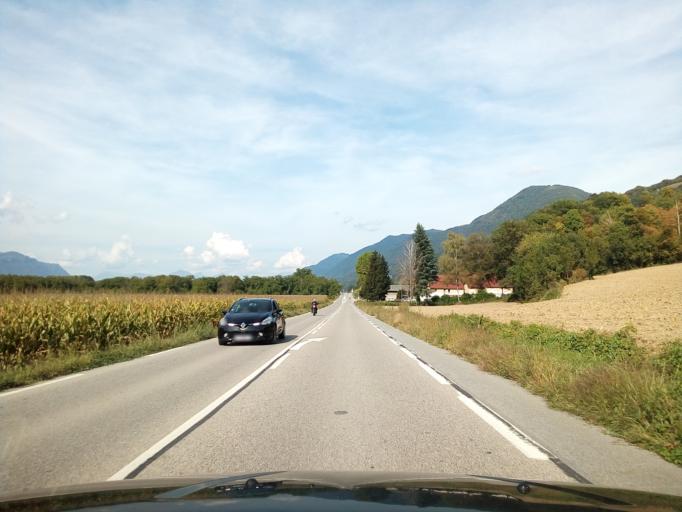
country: FR
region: Rhone-Alpes
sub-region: Departement de l'Isere
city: Le Champ-pres-Froges
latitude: 45.2906
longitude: 5.9409
